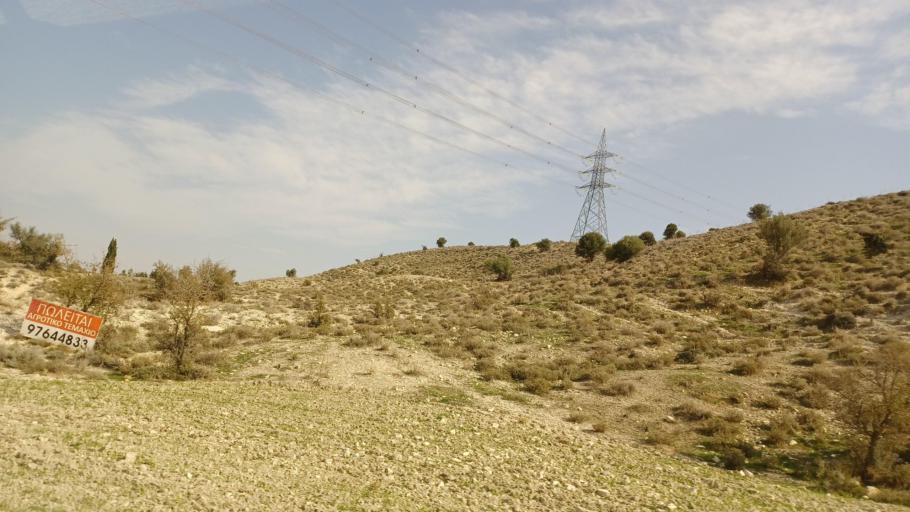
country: CY
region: Lefkosia
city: Lympia
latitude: 34.9819
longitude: 33.4554
